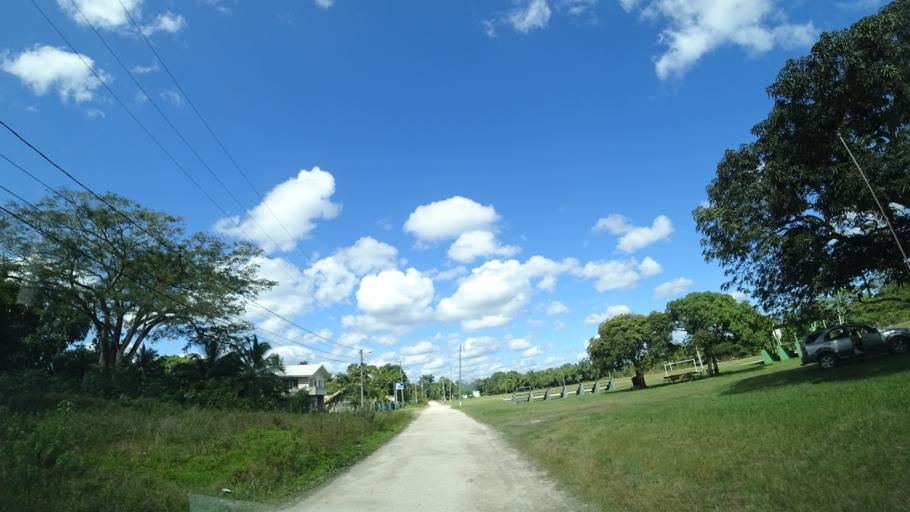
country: BZ
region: Belize
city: Belize City
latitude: 17.5692
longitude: -88.4086
